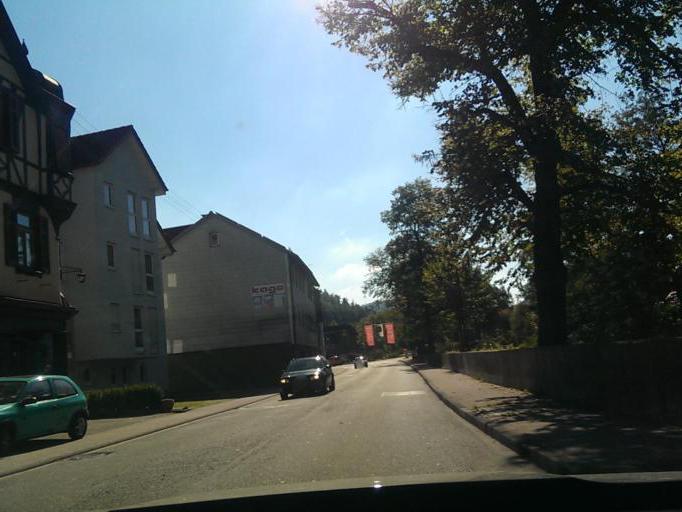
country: DE
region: Baden-Wuerttemberg
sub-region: Karlsruhe Region
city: Hofen an der Enz
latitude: 48.8010
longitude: 8.5834
